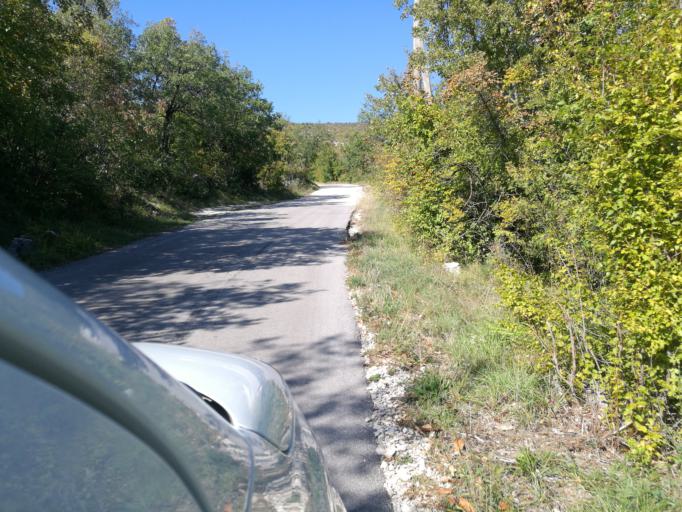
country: HR
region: Splitsko-Dalmatinska
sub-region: Grad Omis
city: Omis
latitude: 43.5144
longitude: 16.7304
